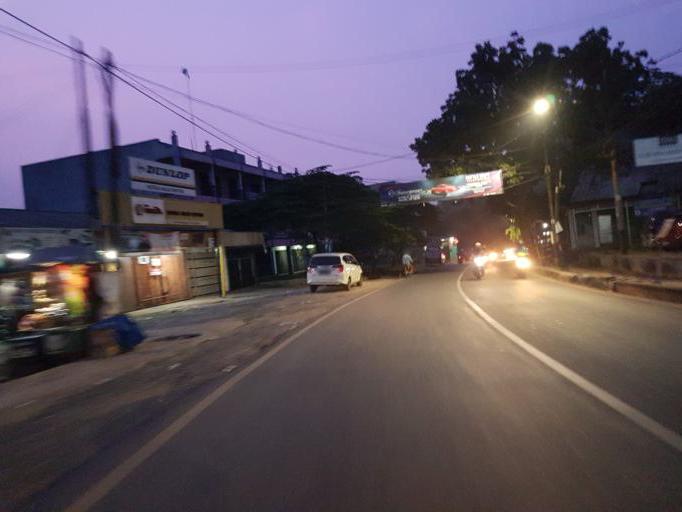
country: ID
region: West Java
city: Serpong
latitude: -6.3143
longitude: 106.6608
